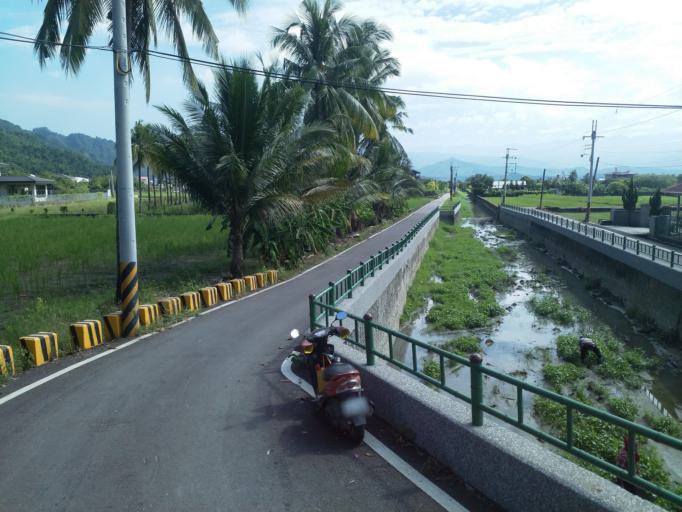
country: TW
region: Taiwan
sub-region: Pingtung
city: Pingtung
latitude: 22.8997
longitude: 120.5176
